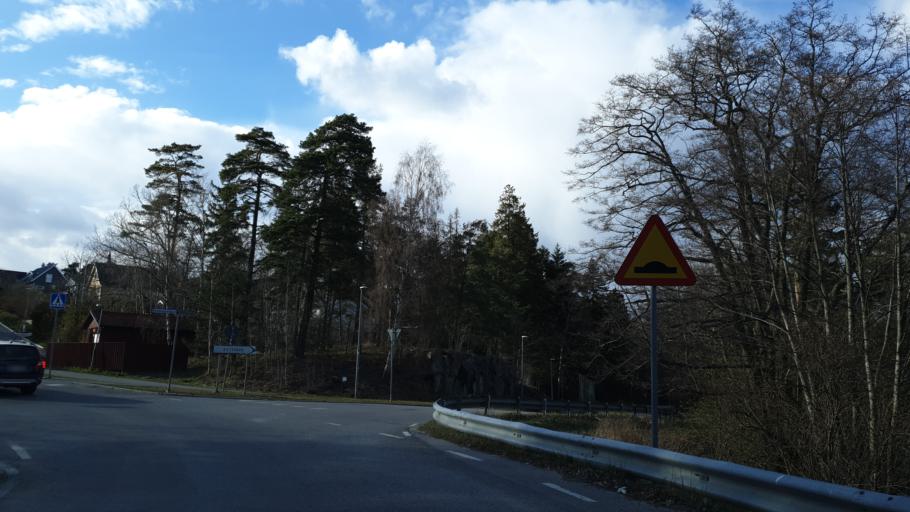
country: SE
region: Stockholm
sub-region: Lidingo
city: Lidingoe
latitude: 59.3833
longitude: 18.1192
